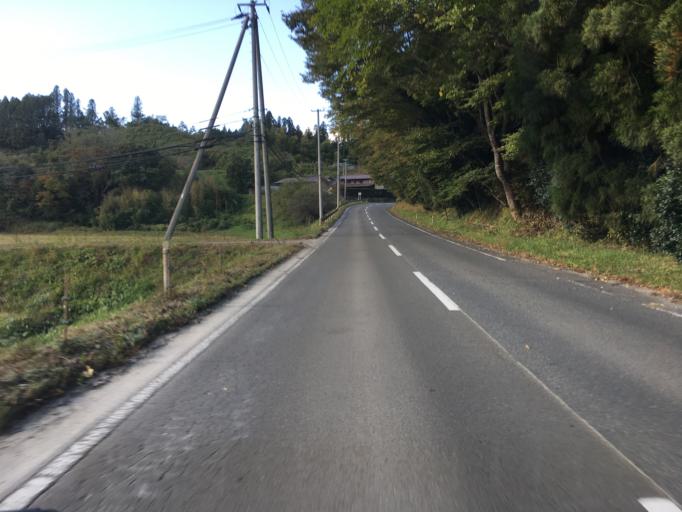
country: JP
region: Miyagi
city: Marumori
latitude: 37.8544
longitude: 140.8307
